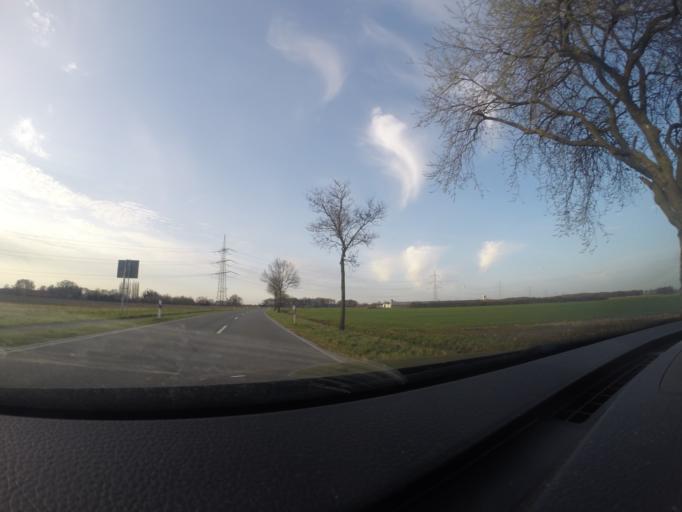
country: DE
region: North Rhine-Westphalia
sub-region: Regierungsbezirk Munster
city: Ahaus
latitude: 52.0964
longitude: 6.9656
